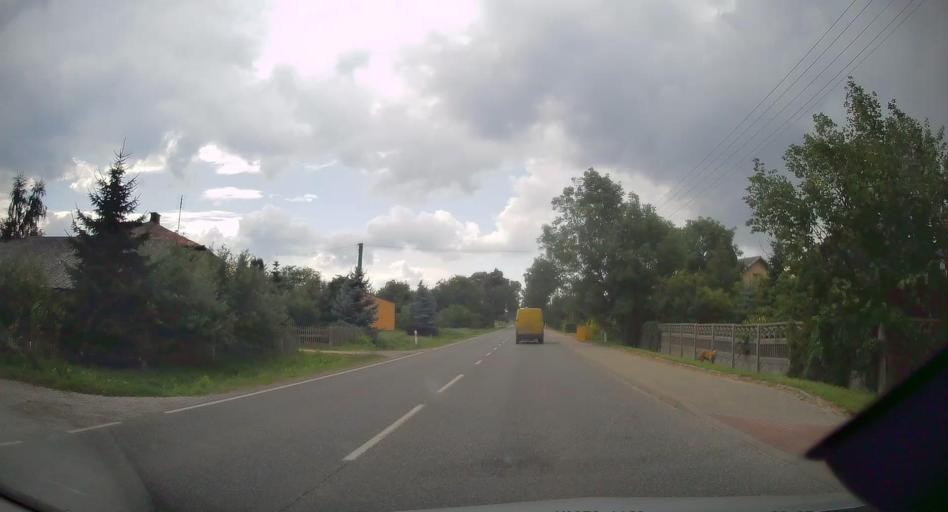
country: PL
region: Lodz Voivodeship
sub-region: Powiat skierniewicki
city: Gluchow
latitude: 51.7746
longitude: 20.1287
